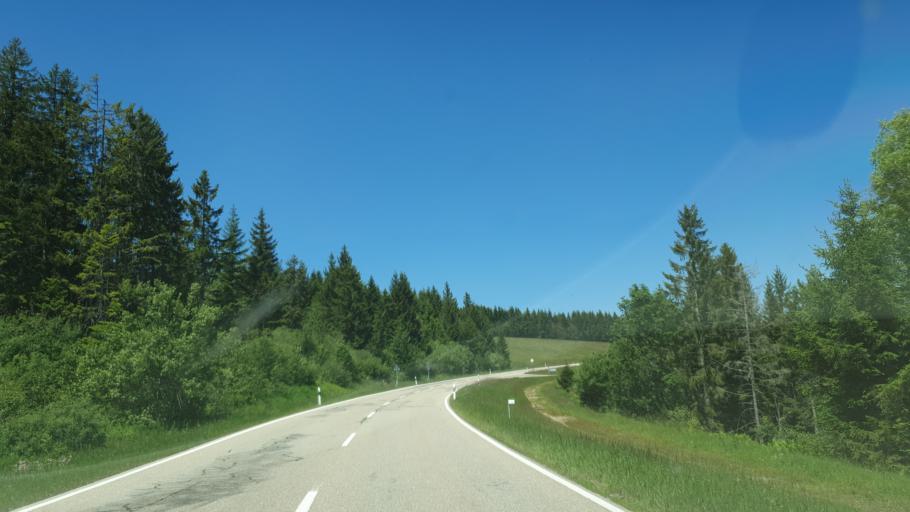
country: DE
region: Baden-Wuerttemberg
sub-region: Freiburg Region
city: Wieden
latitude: 47.8866
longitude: 7.8943
